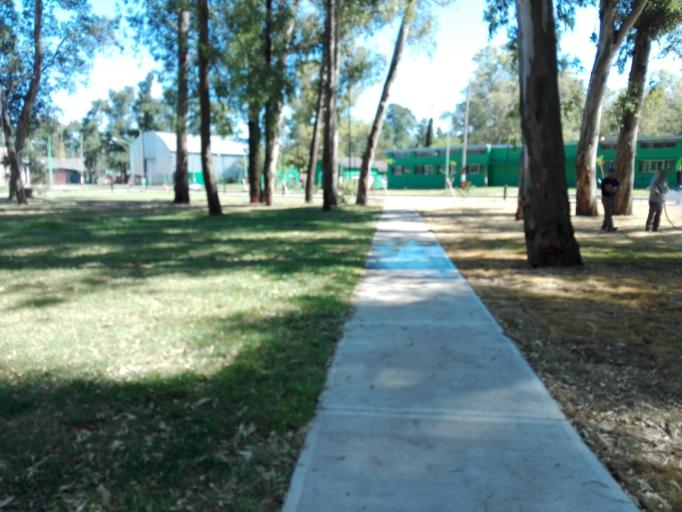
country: AR
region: Buenos Aires
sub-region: Partido de La Plata
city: La Plata
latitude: -34.8933
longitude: -57.9391
